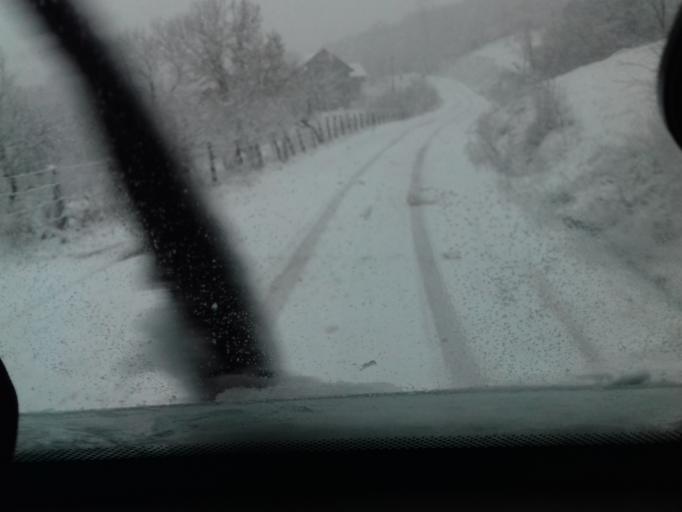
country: BA
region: Federation of Bosnia and Herzegovina
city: Lokvine
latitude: 44.2435
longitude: 17.8049
